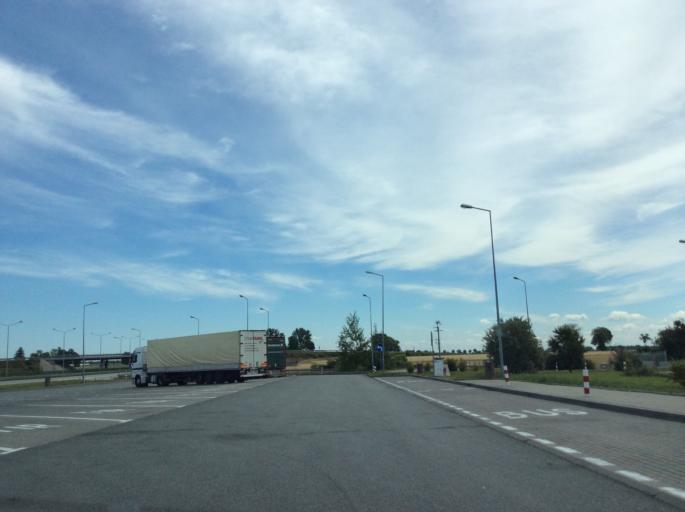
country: PL
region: Greater Poland Voivodeship
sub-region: Powiat poznanski
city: Buk
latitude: 52.3864
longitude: 16.4765
